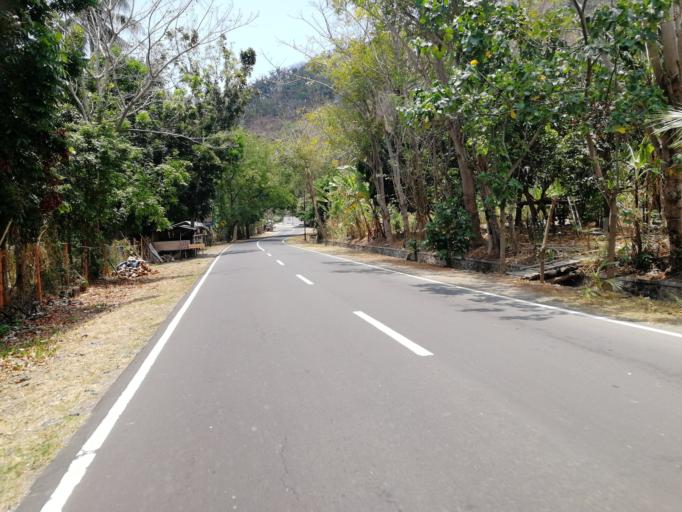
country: ID
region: West Nusa Tenggara
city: Karangsubagan
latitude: -8.4500
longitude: 116.0386
